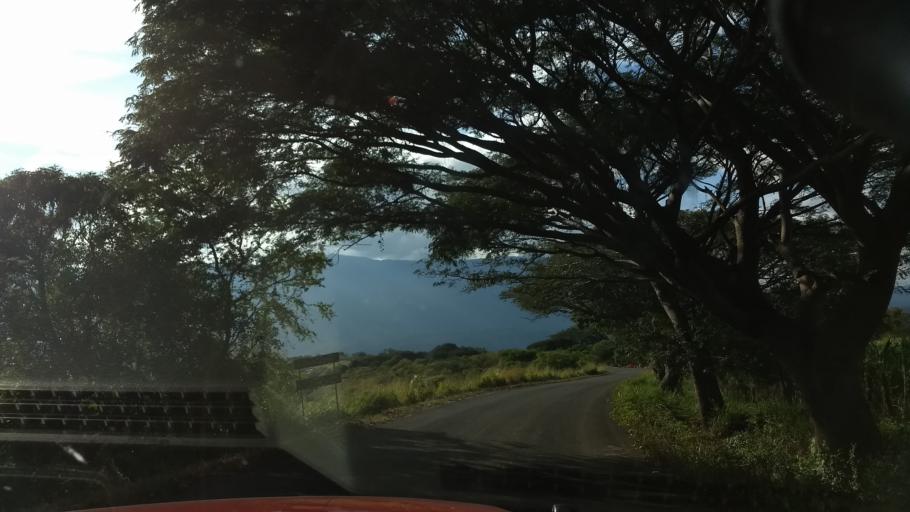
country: MX
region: Colima
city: Suchitlan
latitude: 19.4650
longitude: -103.7788
